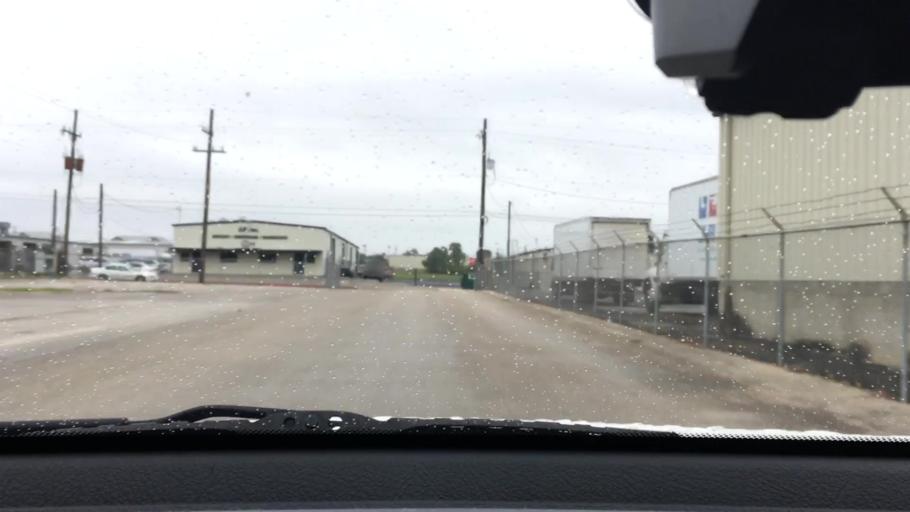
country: US
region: Texas
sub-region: Bexar County
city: Converse
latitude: 29.5121
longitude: -98.3054
